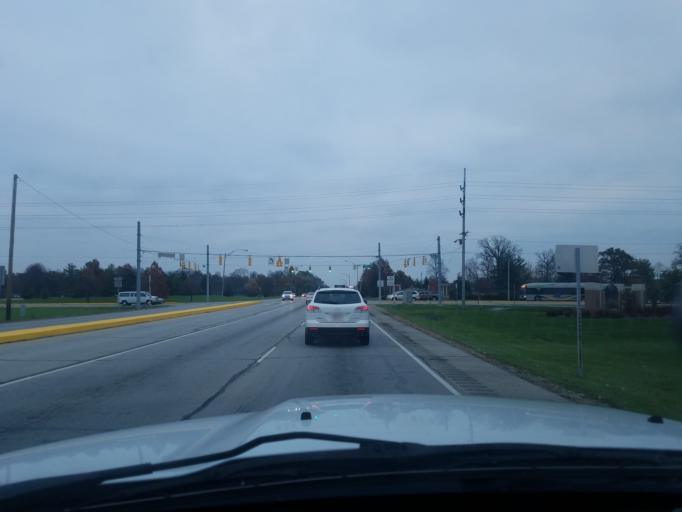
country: US
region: Indiana
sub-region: Delaware County
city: Muncie
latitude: 40.2189
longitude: -85.4210
